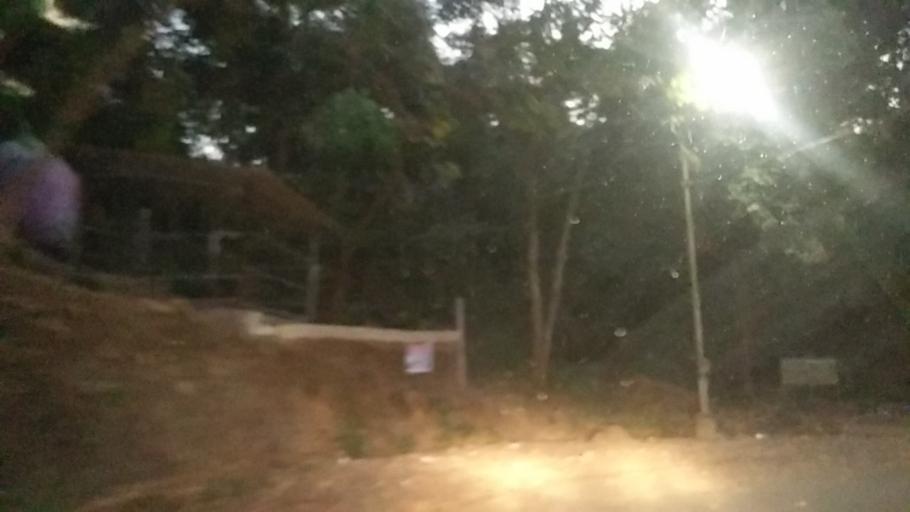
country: IN
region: Goa
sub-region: South Goa
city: Madgaon
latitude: 15.2761
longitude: 73.9683
